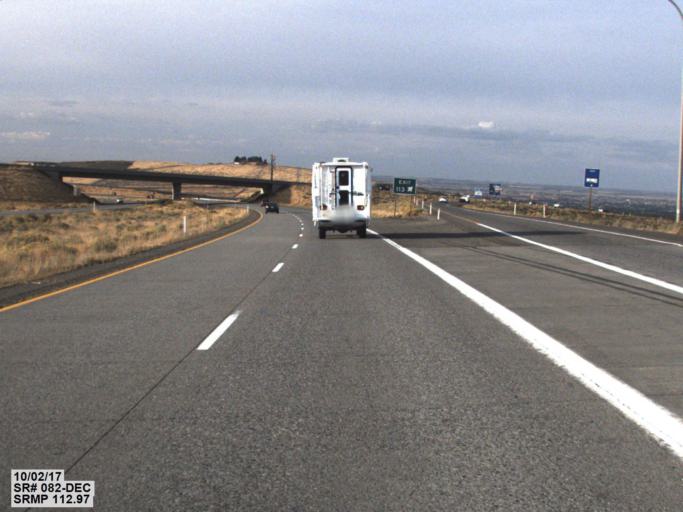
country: US
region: Washington
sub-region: Benton County
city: Kennewick
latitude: 46.1632
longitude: -119.2017
